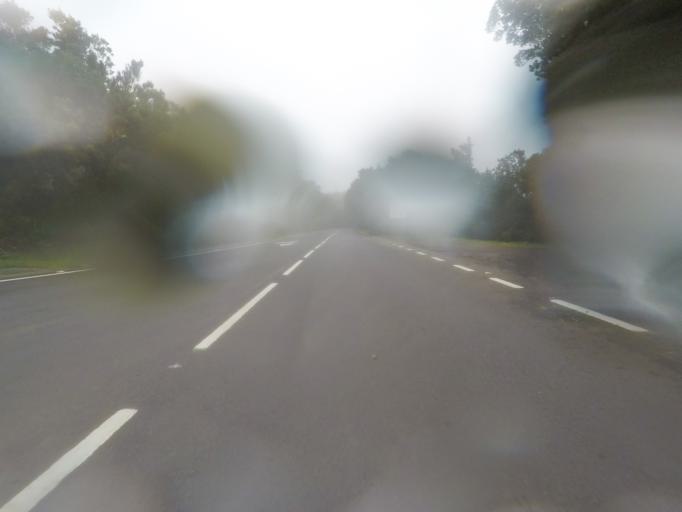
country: ES
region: Canary Islands
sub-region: Provincia de Santa Cruz de Tenerife
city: Vallehermosa
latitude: 28.1358
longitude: -17.2812
